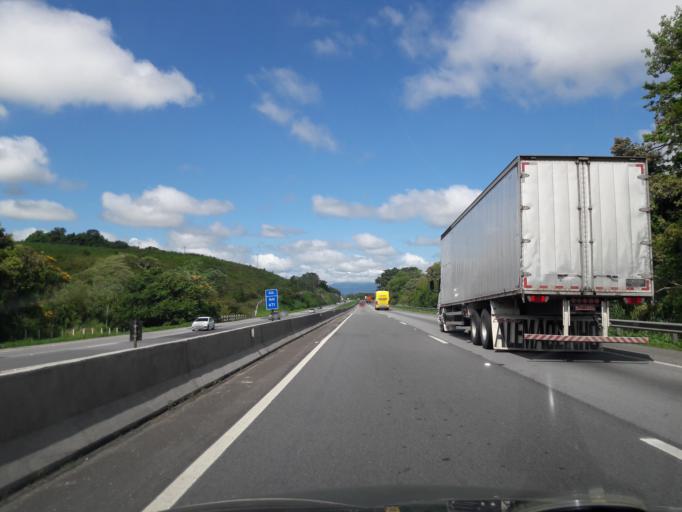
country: BR
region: Sao Paulo
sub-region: Jacupiranga
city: Jacupiranga
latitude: -24.6609
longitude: -47.9699
